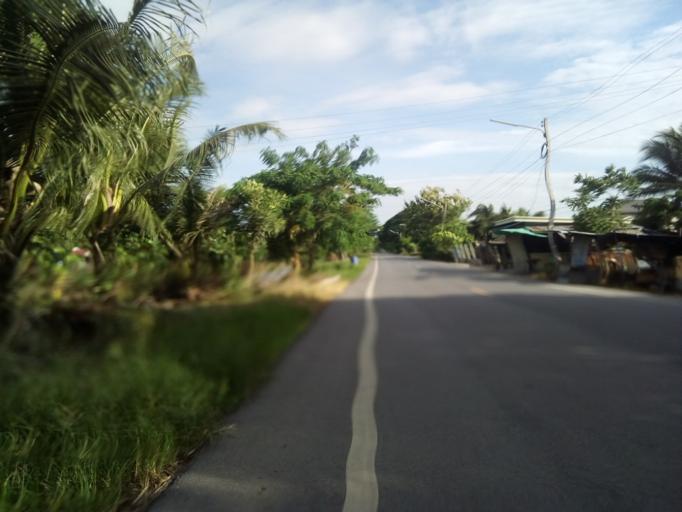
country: TH
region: Pathum Thani
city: Nong Suea
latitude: 14.0984
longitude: 100.8461
